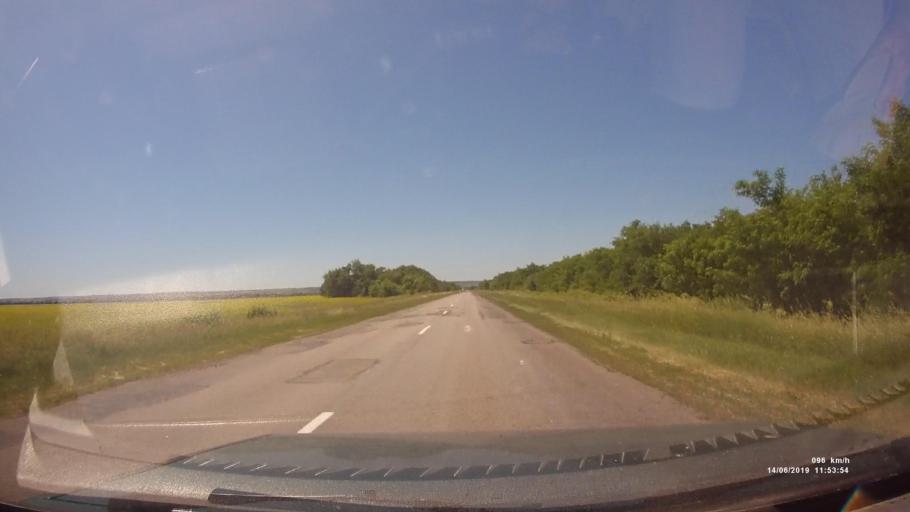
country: RU
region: Rostov
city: Kazanskaya
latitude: 49.8232
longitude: 41.2040
